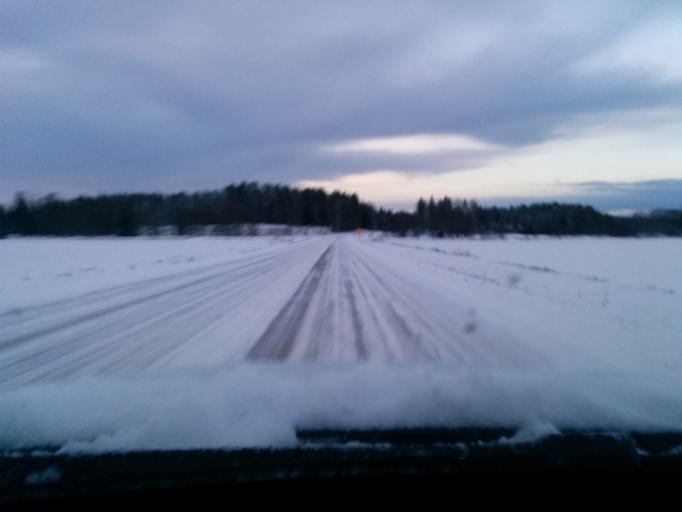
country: SE
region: Uppsala
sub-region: Osthammars Kommun
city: Bjorklinge
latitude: 60.1698
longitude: 17.5714
